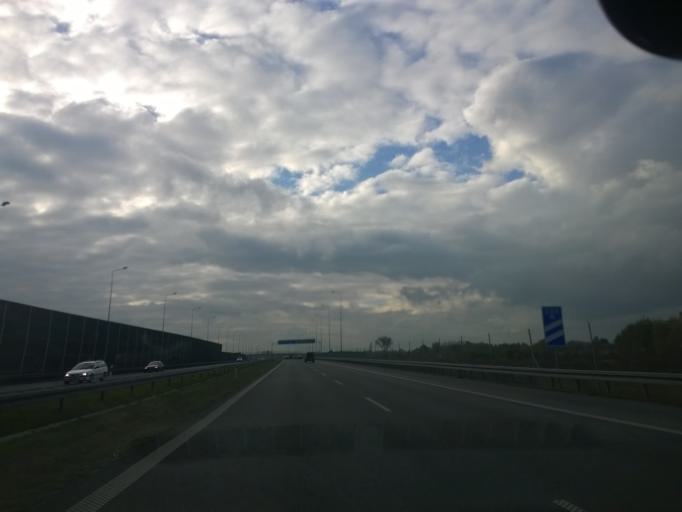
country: PL
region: Masovian Voivodeship
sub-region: Powiat grodziski
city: Grodzisk Mazowiecki
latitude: 52.1477
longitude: 20.6281
